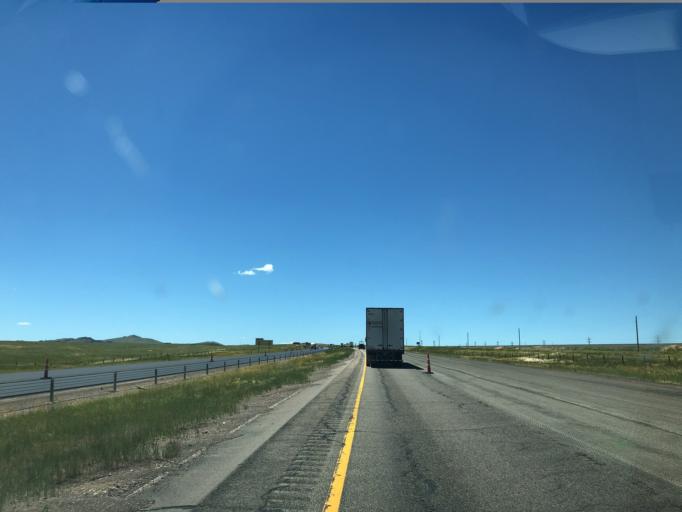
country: US
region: Wyoming
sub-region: Laramie County
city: Cheyenne
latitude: 41.0988
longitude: -105.1209
